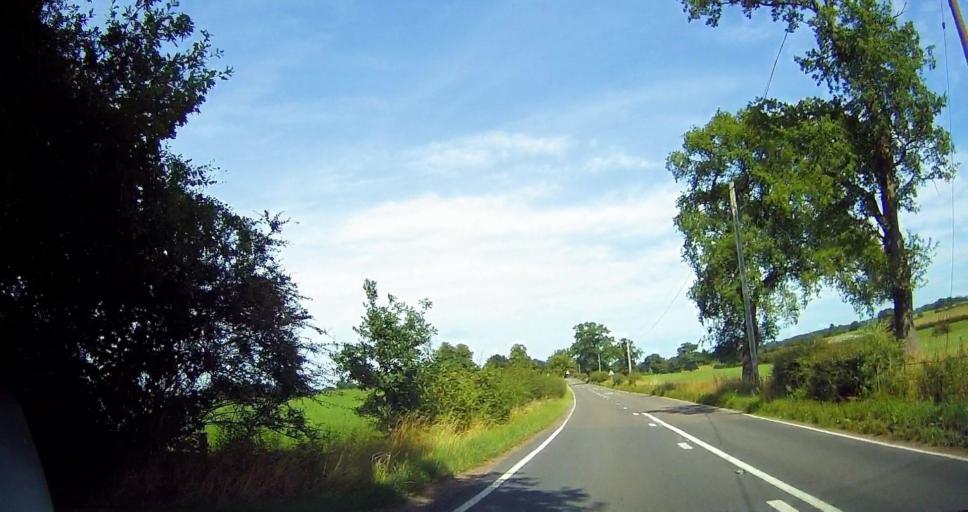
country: GB
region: England
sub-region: Shropshire
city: Market Drayton
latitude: 52.9494
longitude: -2.5093
